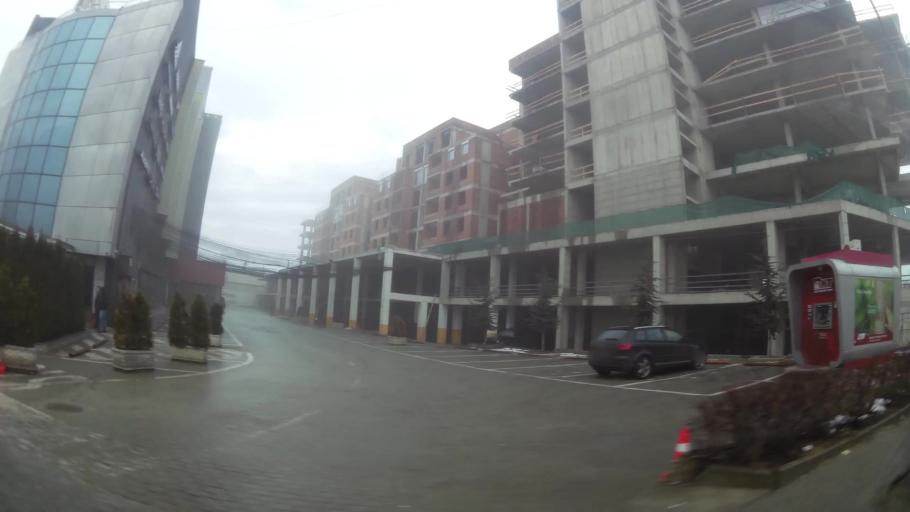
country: XK
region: Pristina
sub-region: Komuna e Prishtines
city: Pristina
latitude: 42.6610
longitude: 21.1422
